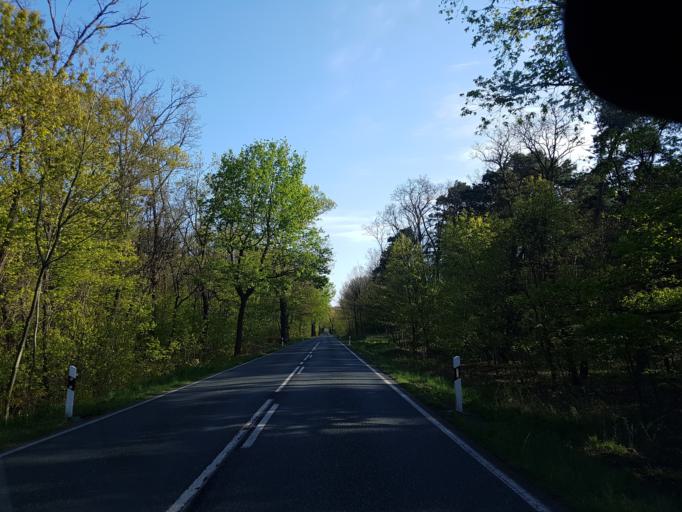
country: DE
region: Brandenburg
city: Altdobern
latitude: 51.6310
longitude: 14.0294
